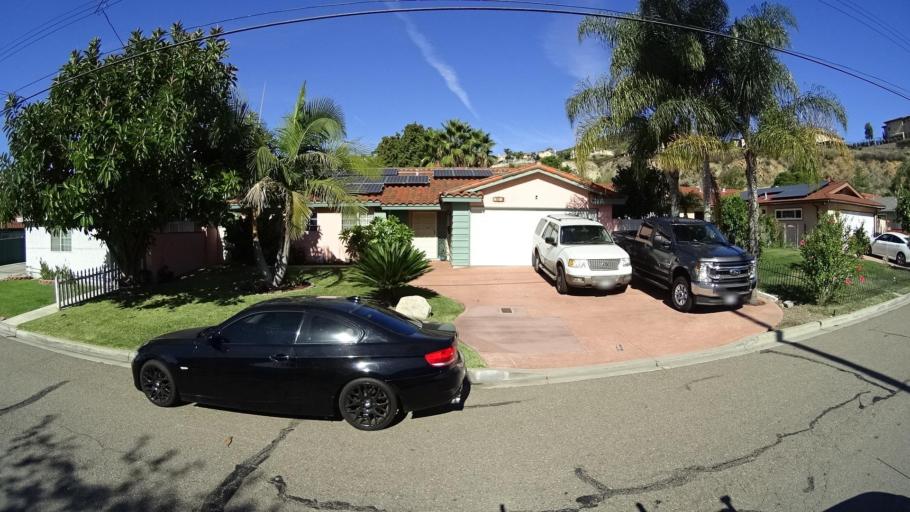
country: US
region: California
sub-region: San Diego County
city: La Presa
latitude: 32.7199
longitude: -116.9753
